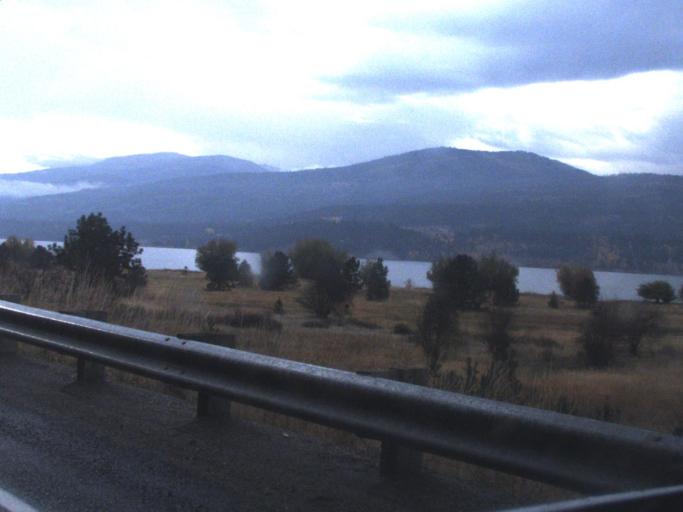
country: US
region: Washington
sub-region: Stevens County
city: Kettle Falls
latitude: 48.5691
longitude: -118.1114
